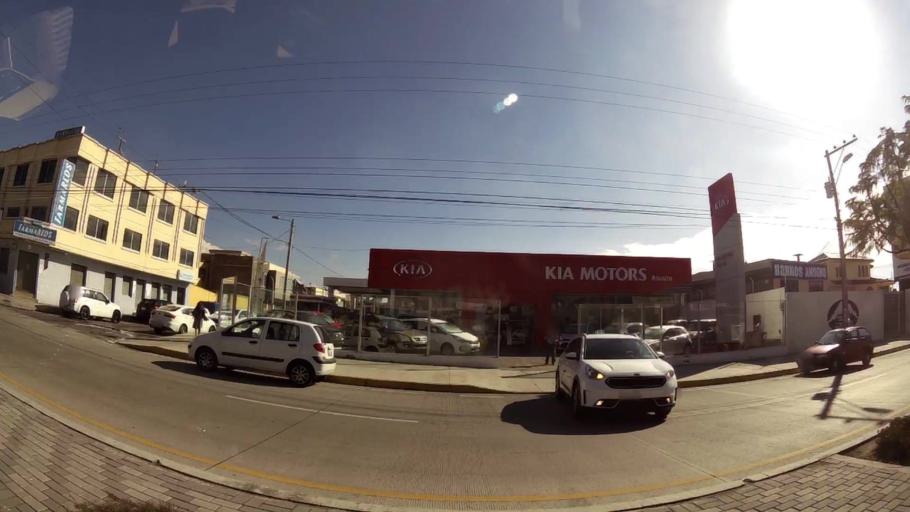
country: EC
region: Chimborazo
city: Riobamba
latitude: -1.6520
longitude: -78.6680
